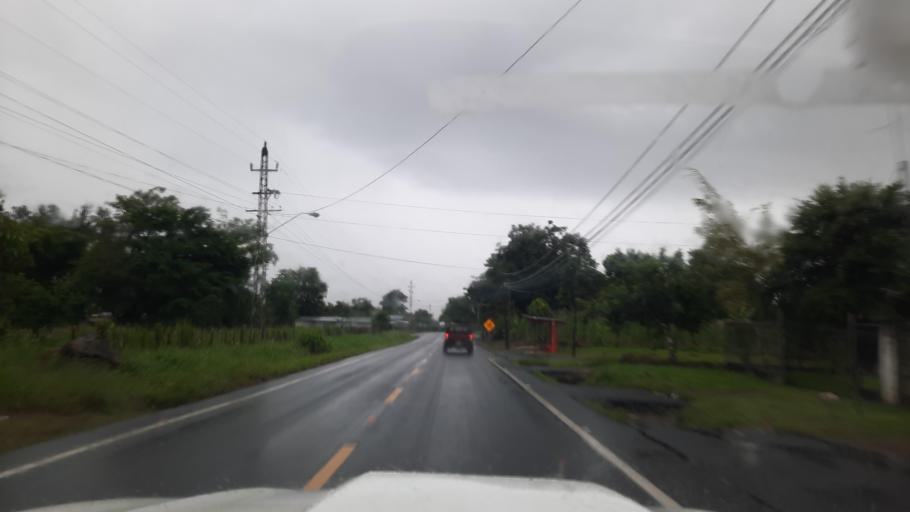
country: PA
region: Chiriqui
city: Sortova
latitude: 8.5514
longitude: -82.6261
